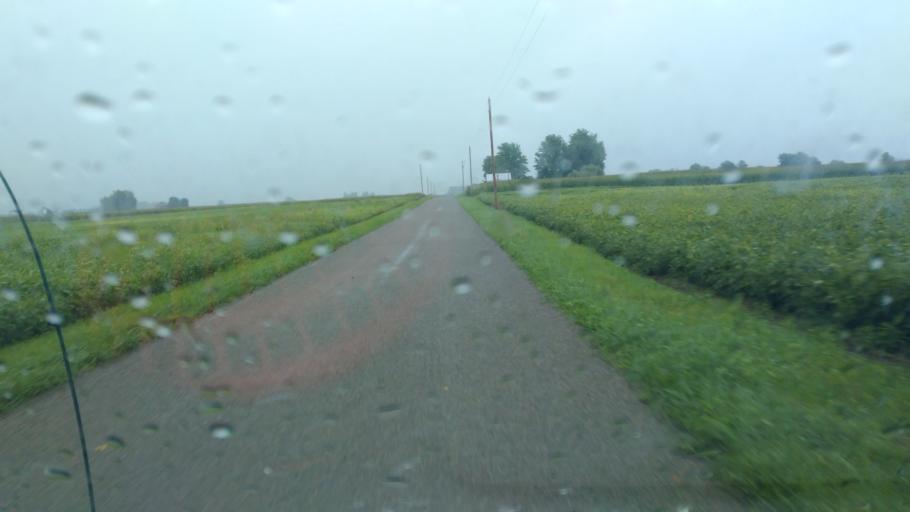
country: US
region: Ohio
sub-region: Hardin County
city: Kenton
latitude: 40.7124
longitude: -83.5951
